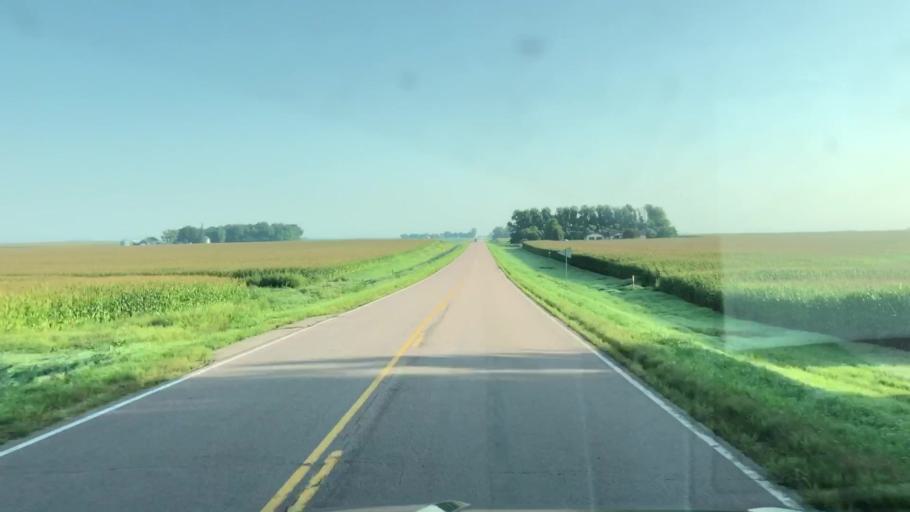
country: US
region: Iowa
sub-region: Lyon County
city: George
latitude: 43.2945
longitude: -95.9994
